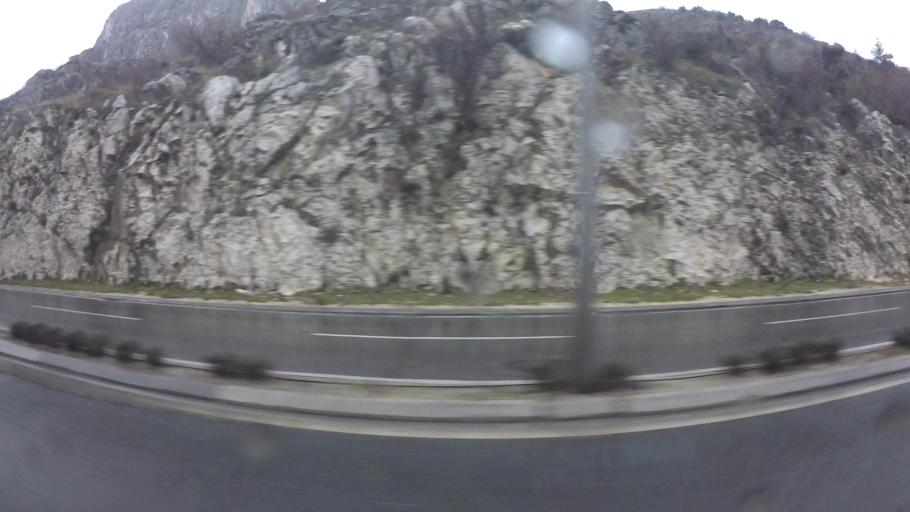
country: BA
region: Federation of Bosnia and Herzegovina
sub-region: Hercegovacko-Bosanski Kanton
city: Mostar
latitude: 43.3321
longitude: 17.8149
